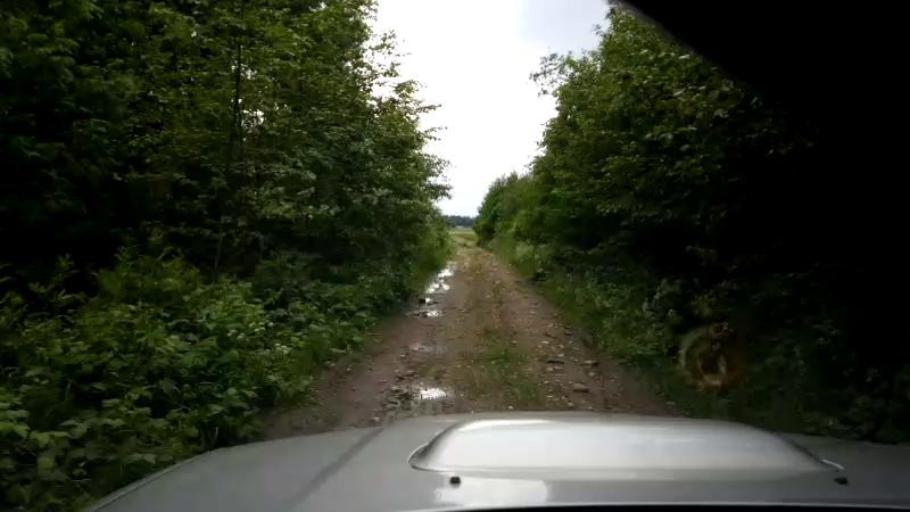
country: EE
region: Paernumaa
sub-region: Halinga vald
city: Parnu-Jaagupi
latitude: 58.5657
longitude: 24.5609
